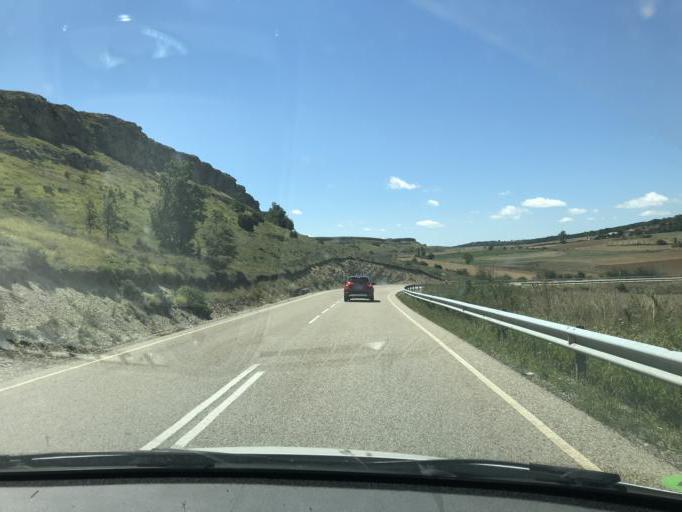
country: ES
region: Castille and Leon
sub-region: Provincia de Palencia
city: Dehesa de Montejo
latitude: 42.8238
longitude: -4.4970
